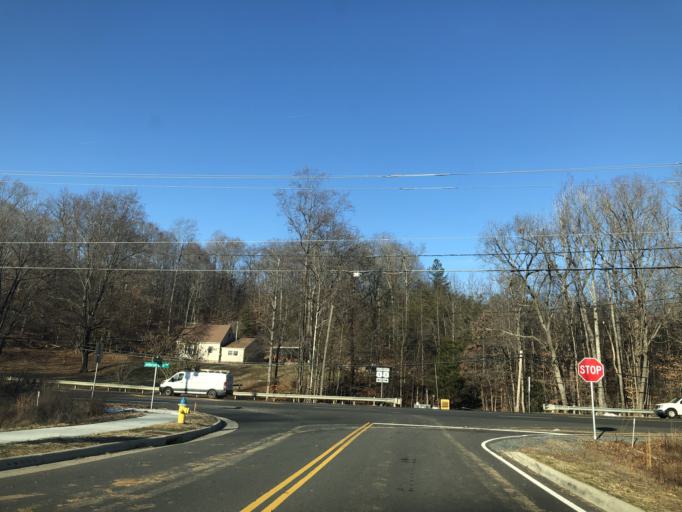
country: US
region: Virginia
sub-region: Stafford County
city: Stafford
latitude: 38.4094
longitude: -77.4141
